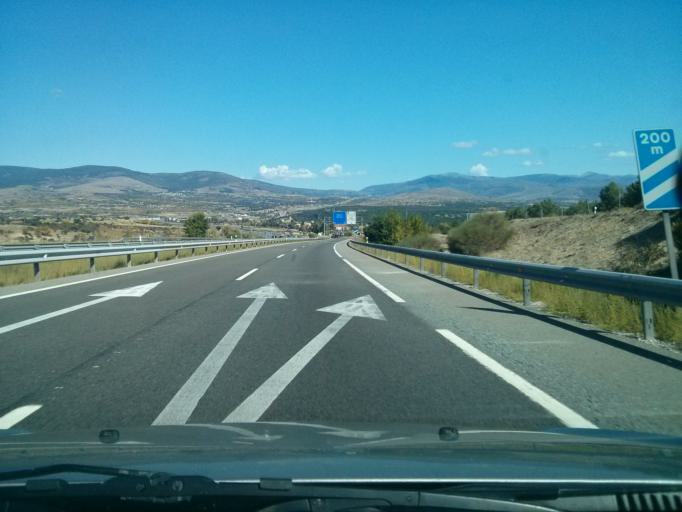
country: ES
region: Madrid
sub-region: Provincia de Madrid
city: Buitrago del Lozoya
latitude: 40.9737
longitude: -3.6396
